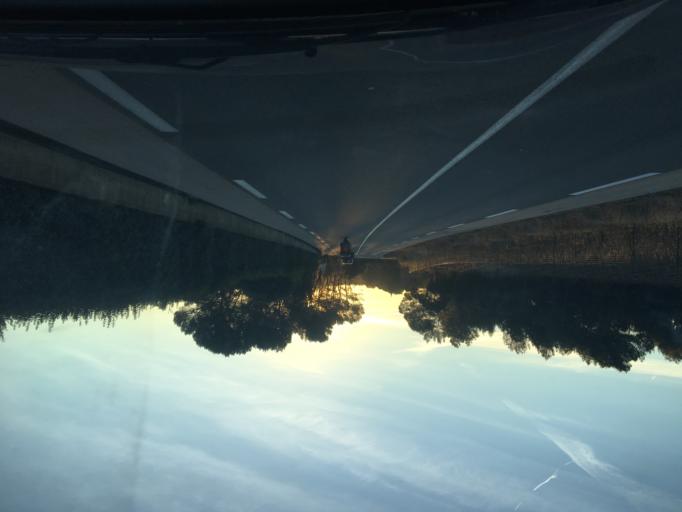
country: FR
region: Provence-Alpes-Cote d'Azur
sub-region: Departement du Var
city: Taradeau
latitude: 43.4622
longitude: 6.4029
